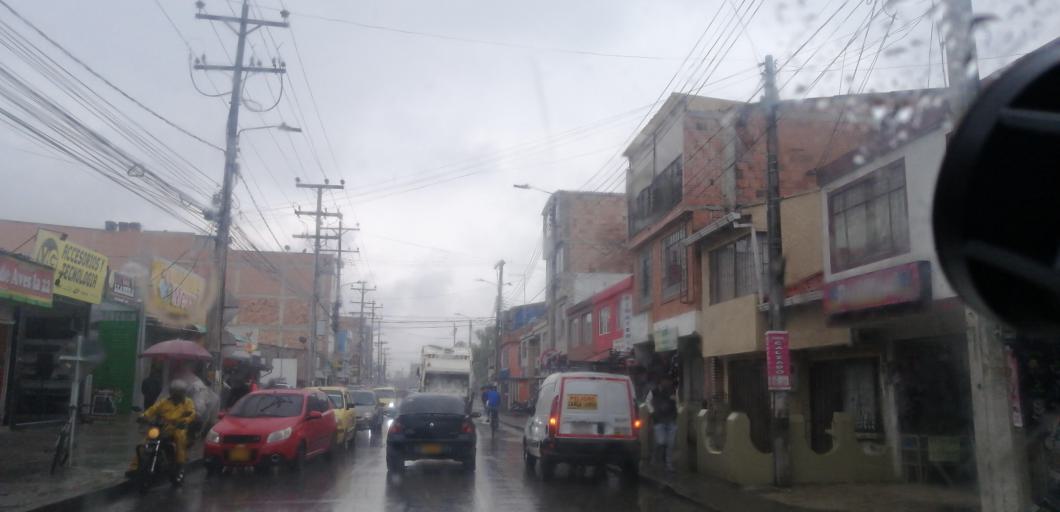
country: CO
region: Cundinamarca
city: Madrid
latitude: 4.7356
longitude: -74.2585
